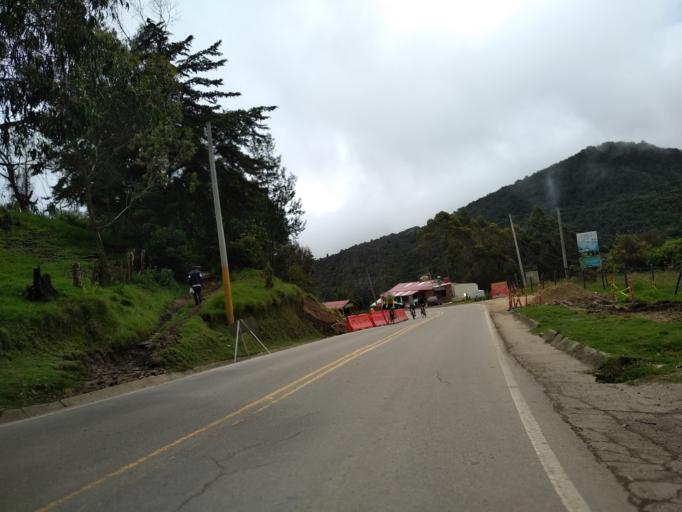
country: CO
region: Bogota D.C.
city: Barrio San Luis
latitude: 4.6620
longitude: -74.0048
